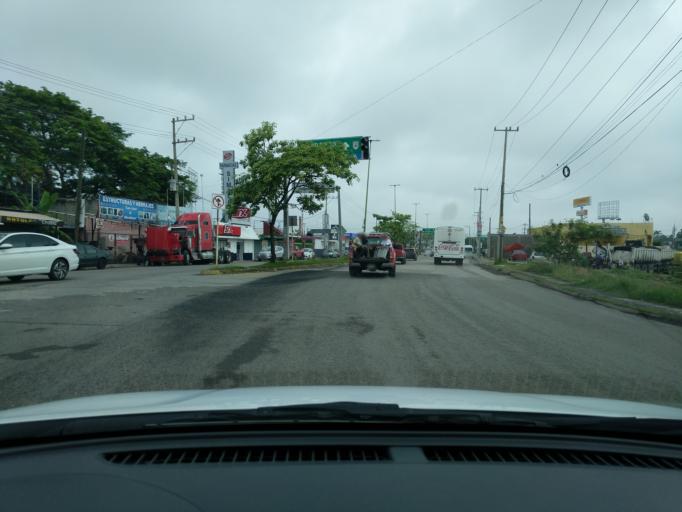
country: MX
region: Tabasco
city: Villahermosa
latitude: 17.9642
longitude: -92.9628
